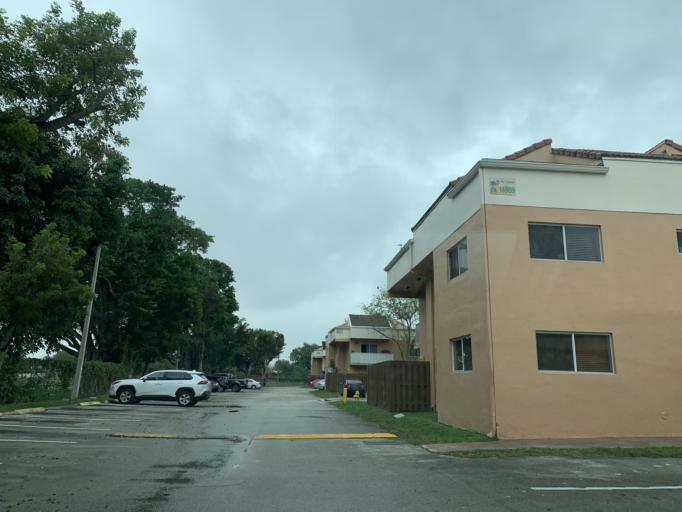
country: US
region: Florida
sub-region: Miami-Dade County
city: Kendall West
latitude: 25.6942
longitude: -80.4349
